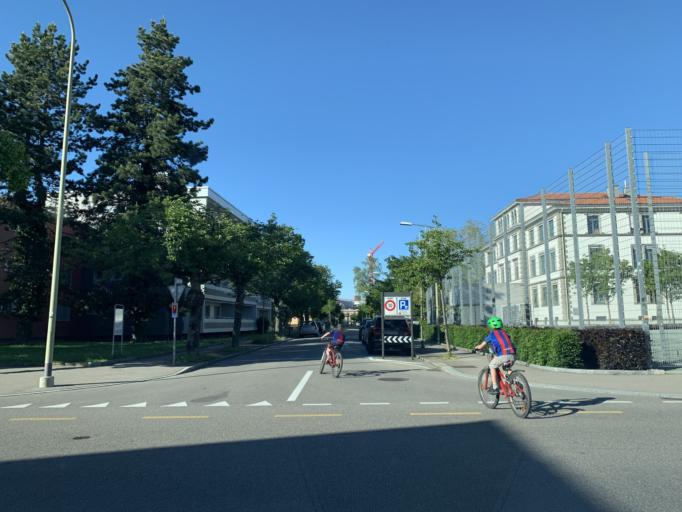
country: CH
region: Zurich
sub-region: Bezirk Winterthur
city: Stadt Winterthur (Kreis 1) / Toessfeld
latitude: 47.4927
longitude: 8.7124
